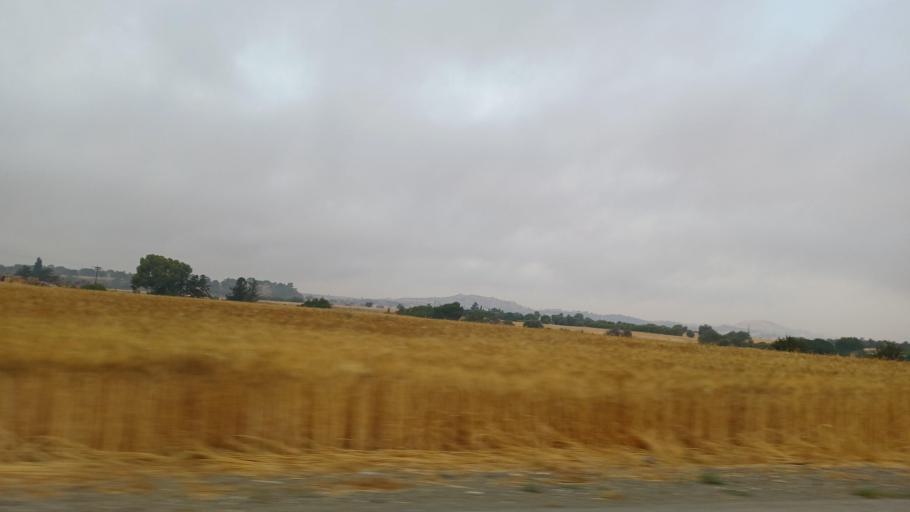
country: CY
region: Larnaka
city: Tersefanou
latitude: 34.8354
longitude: 33.5080
